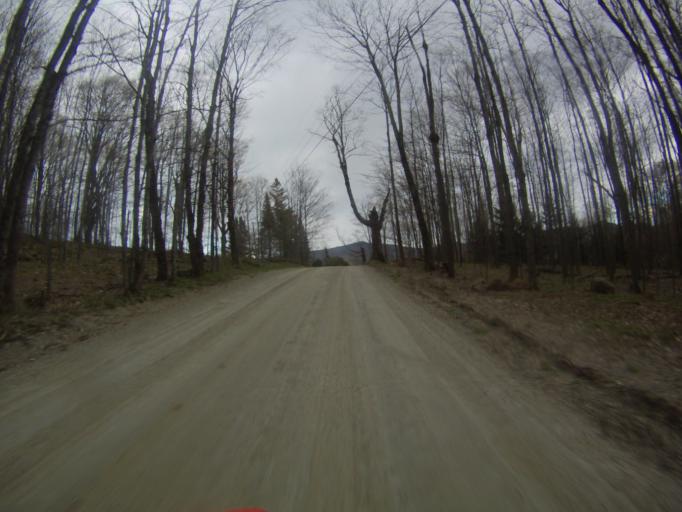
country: US
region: Vermont
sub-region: Addison County
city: Bristol
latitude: 44.0573
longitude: -73.0217
